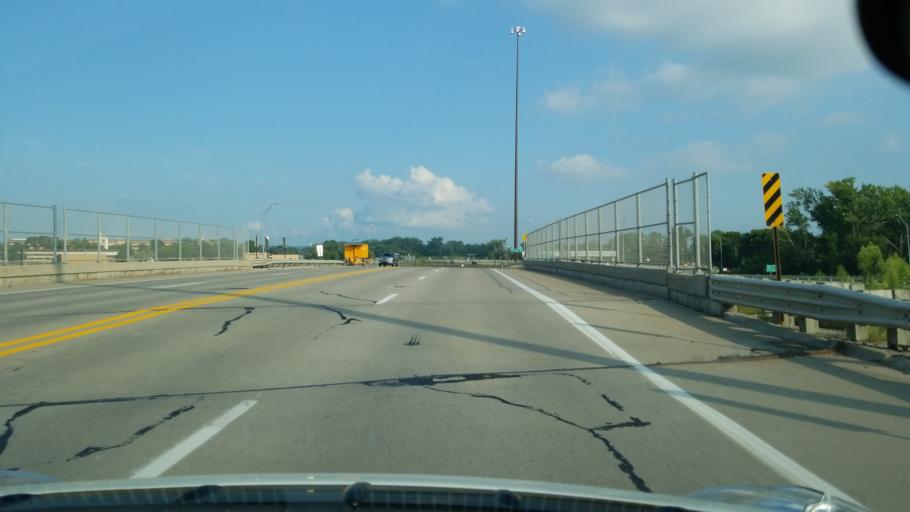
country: US
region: Nebraska
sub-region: Sarpy County
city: Offutt Air Force Base
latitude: 41.1147
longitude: -95.9271
